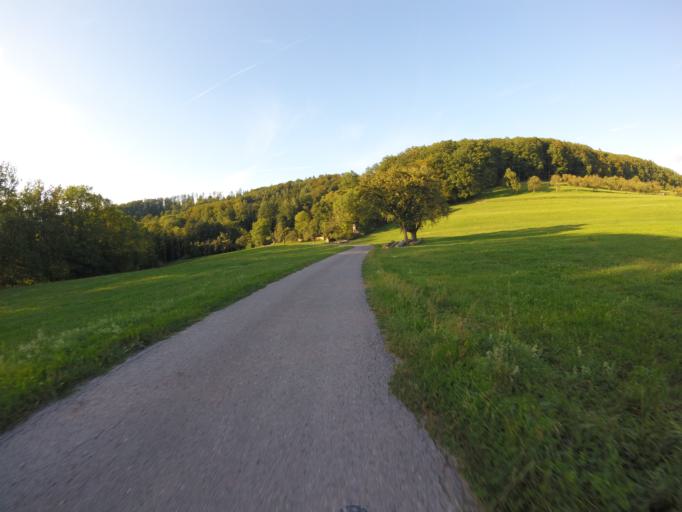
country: DE
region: Baden-Wuerttemberg
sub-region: Regierungsbezirk Stuttgart
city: Oppenweiler
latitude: 49.0051
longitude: 9.4439
